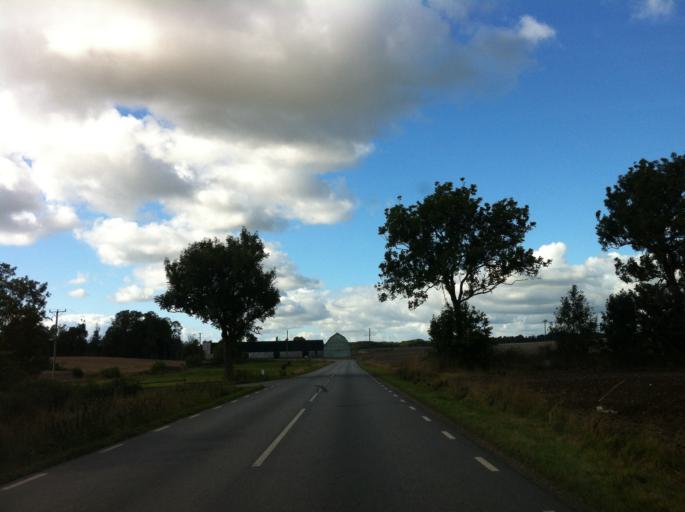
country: SE
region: Skane
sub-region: Tomelilla Kommun
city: Tomelilla
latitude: 55.6479
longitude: 13.9668
